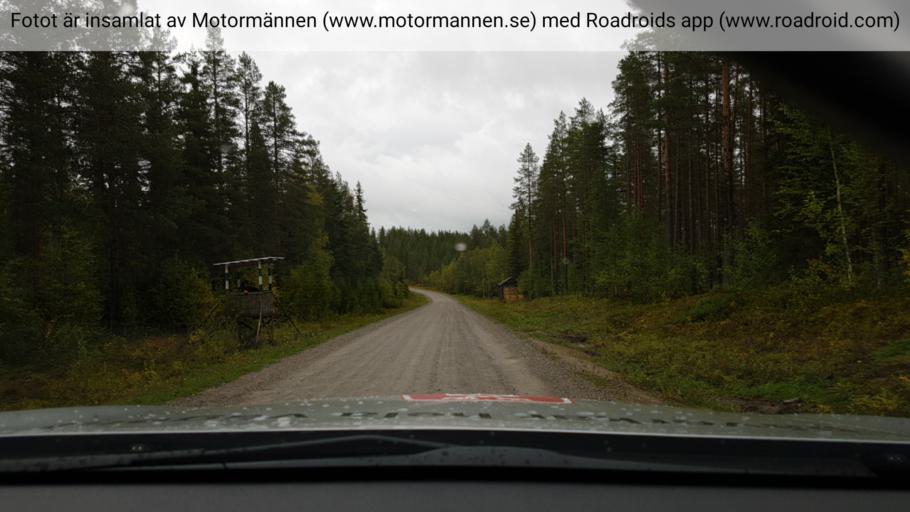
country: SE
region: Vaesterbotten
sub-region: Skelleftea Kommun
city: Boliden
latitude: 65.0656
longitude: 20.4931
